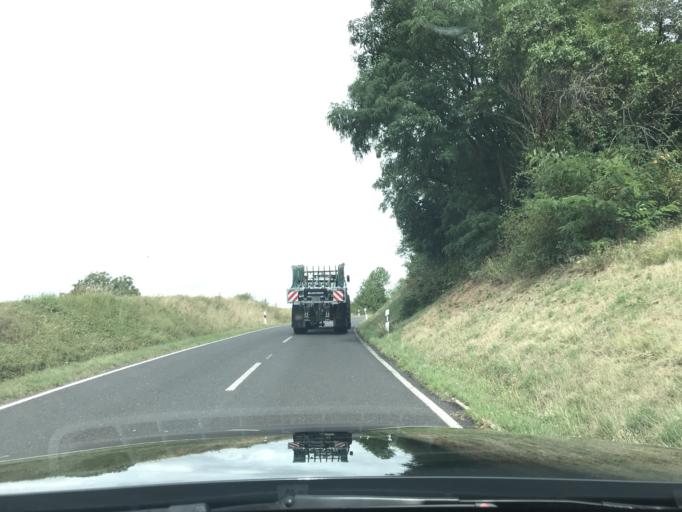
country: DE
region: Bavaria
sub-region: Regierungsbezirk Unterfranken
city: Kirchlauter
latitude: 50.0574
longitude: 10.6693
